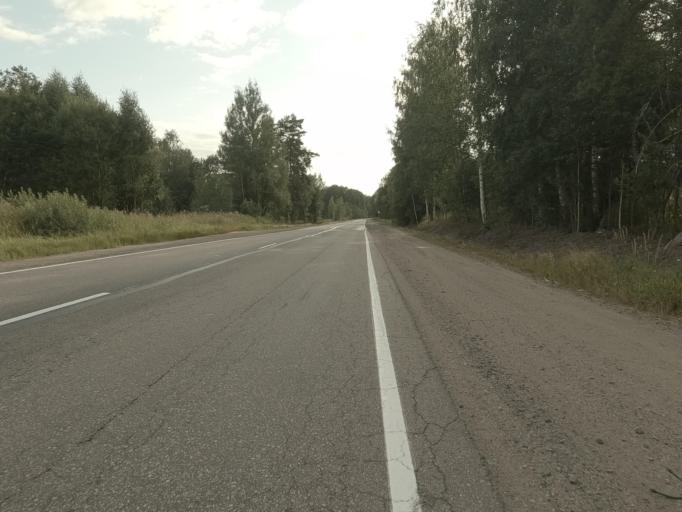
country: RU
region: Leningrad
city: Kamennogorsk
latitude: 60.8743
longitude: 28.9989
